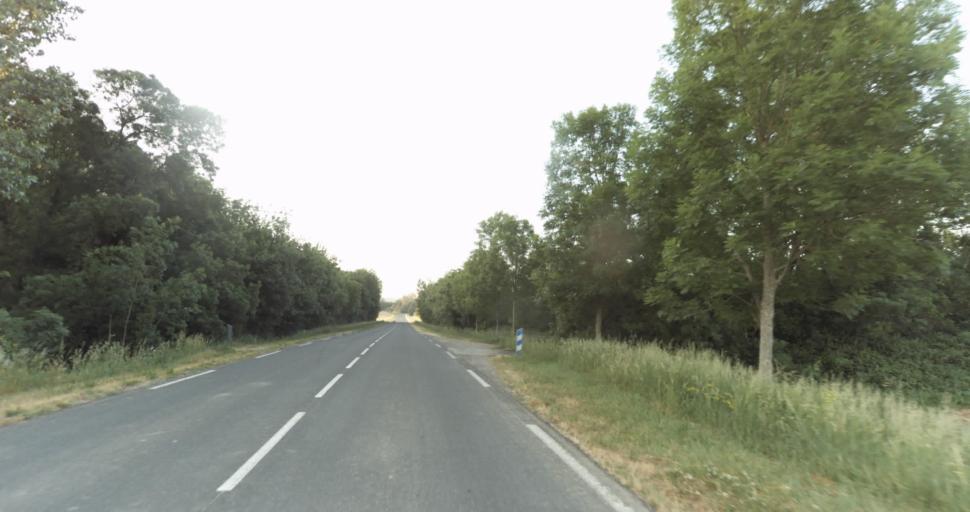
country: FR
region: Midi-Pyrenees
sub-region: Departement du Gers
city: Pujaudran
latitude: 43.6425
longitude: 1.1410
